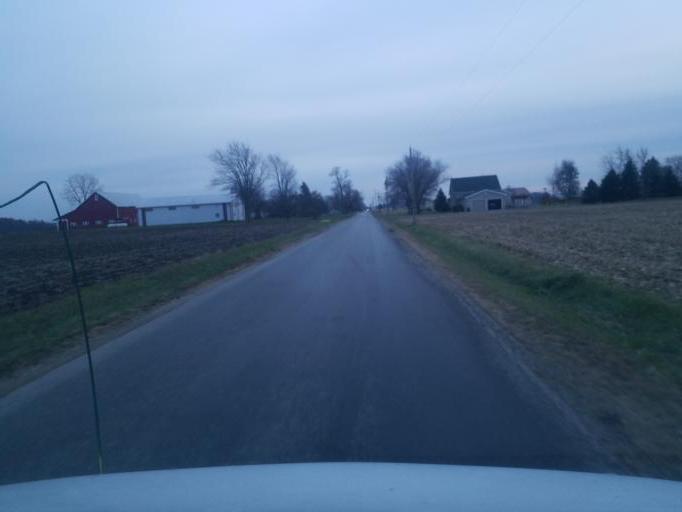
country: US
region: Indiana
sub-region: Adams County
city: Decatur
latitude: 40.7867
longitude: -85.0149
